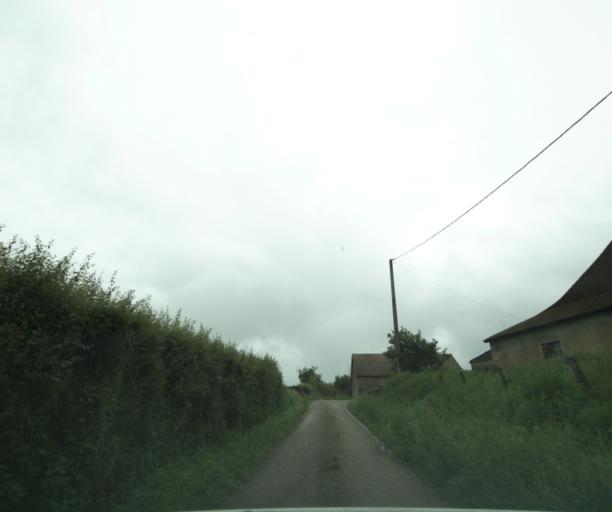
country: FR
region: Bourgogne
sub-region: Departement de Saone-et-Loire
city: Charolles
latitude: 46.4641
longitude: 4.3182
